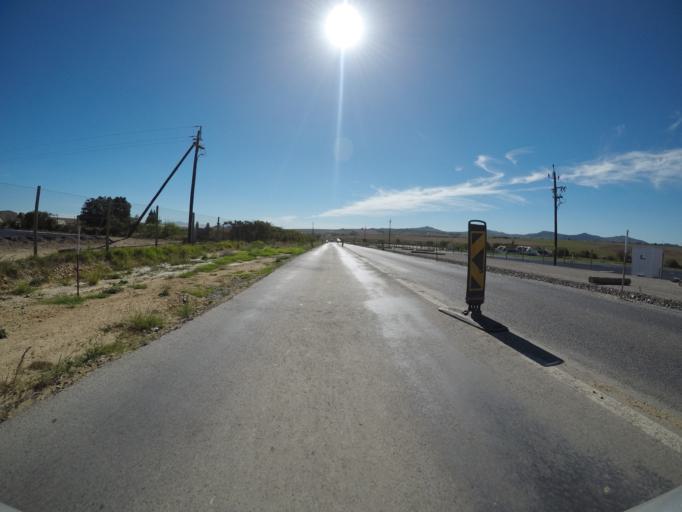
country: ZA
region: Western Cape
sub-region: Cape Winelands District Municipality
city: Stellenbosch
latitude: -33.9913
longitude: 18.8108
